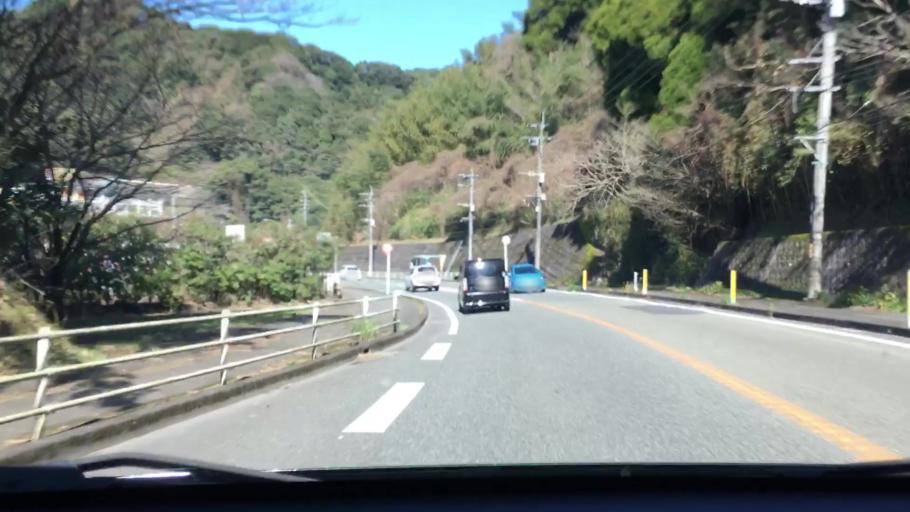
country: JP
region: Kagoshima
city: Kagoshima-shi
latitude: 31.6373
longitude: 130.5194
